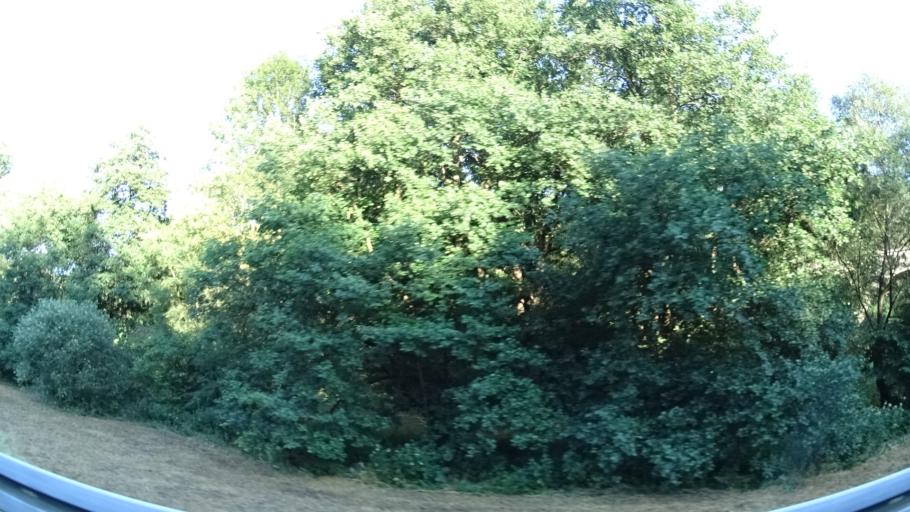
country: DE
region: Bavaria
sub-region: Regierungsbezirk Unterfranken
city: Mellrichstadt
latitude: 50.4462
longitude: 10.3306
